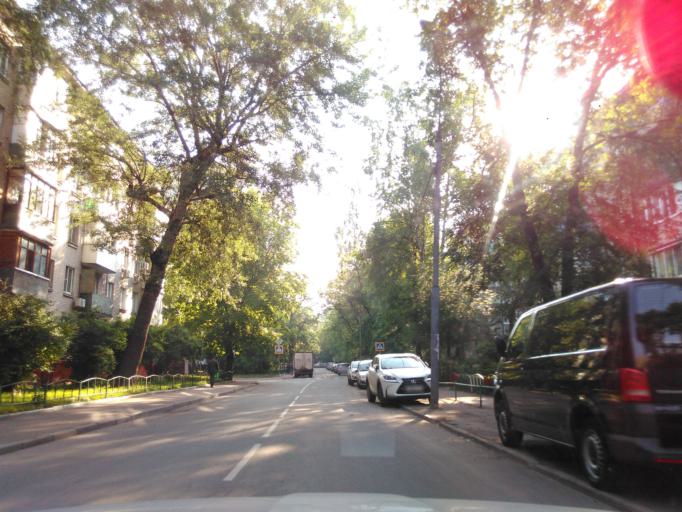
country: RU
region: Moskovskaya
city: Koptevo
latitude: 55.8167
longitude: 37.4937
